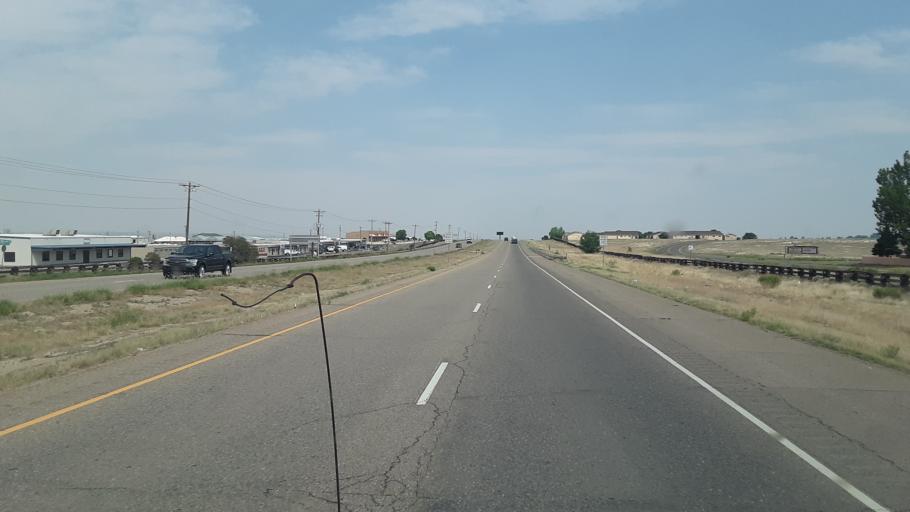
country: US
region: Colorado
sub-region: Pueblo County
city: Pueblo West
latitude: 38.3329
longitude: -104.7341
